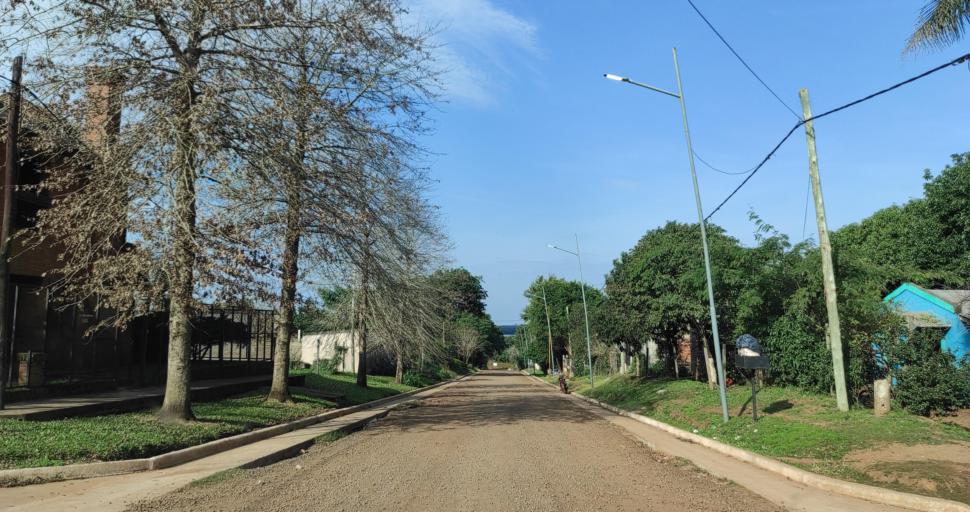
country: AR
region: Corrientes
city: Santo Tome
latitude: -28.5523
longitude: -56.0303
